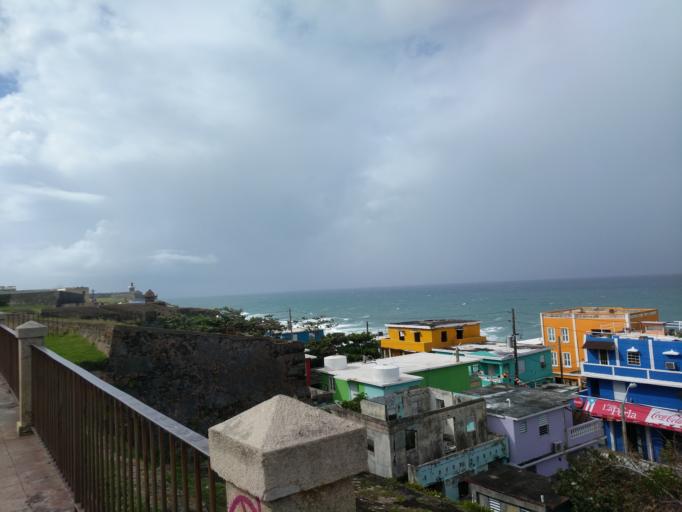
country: PR
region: San Juan
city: San Juan
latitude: 18.4682
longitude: -66.1162
